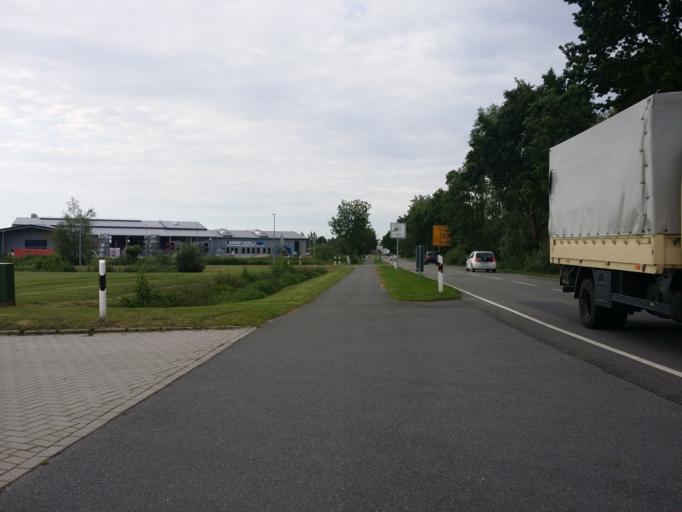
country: DE
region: Lower Saxony
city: Wittmund
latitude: 53.5826
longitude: 7.7819
